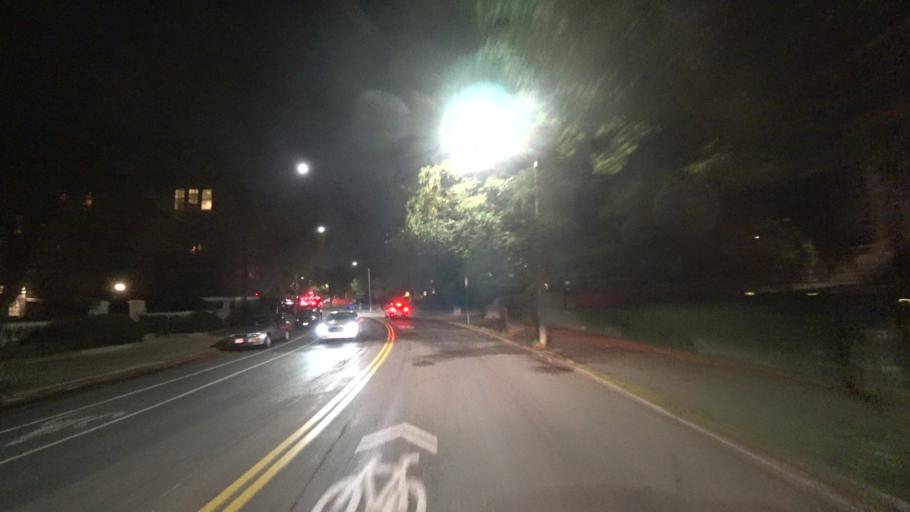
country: US
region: Massachusetts
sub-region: Norfolk County
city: Brookline
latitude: 42.3353
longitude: -71.1248
